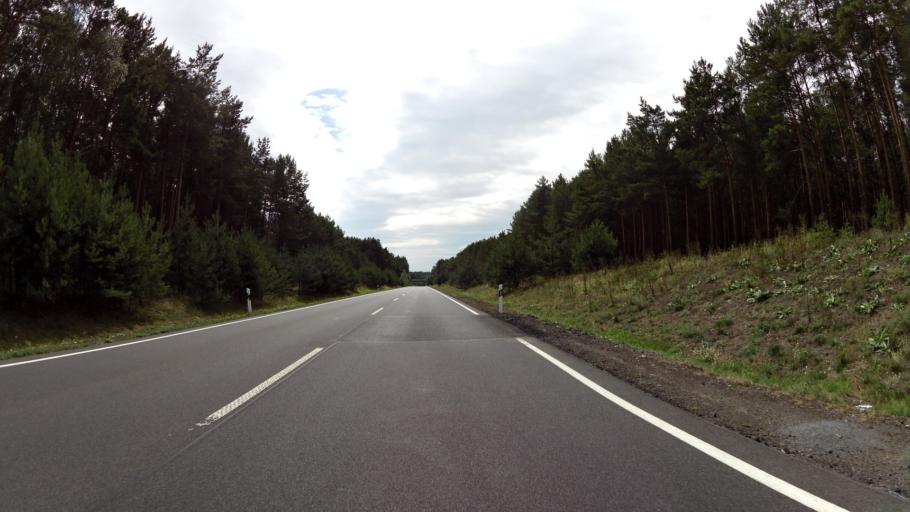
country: DE
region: Brandenburg
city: Schenkendobern
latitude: 51.9895
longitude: 14.6581
